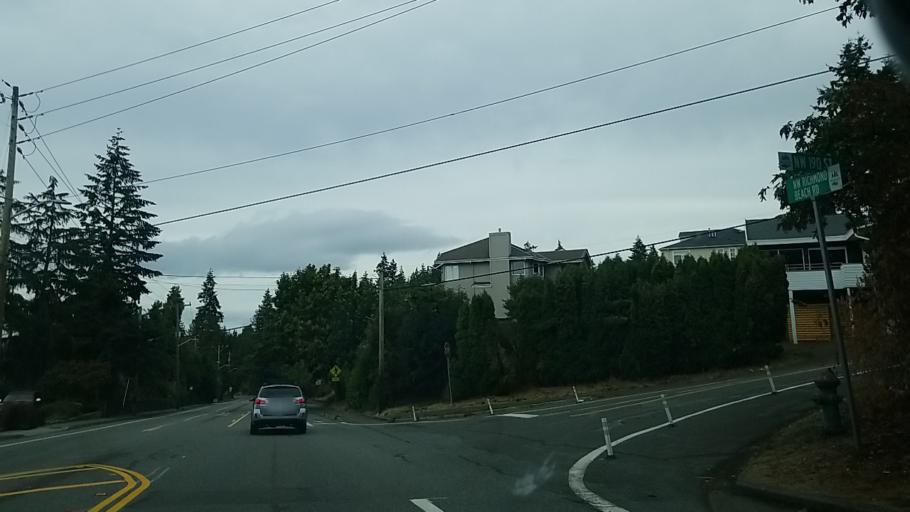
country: US
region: Washington
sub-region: Snohomish County
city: Esperance
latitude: 47.7667
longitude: -122.3709
